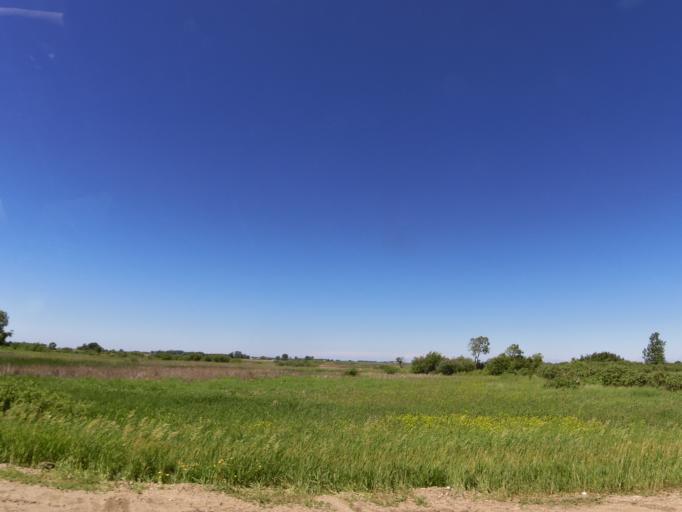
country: US
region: Minnesota
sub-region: Mahnomen County
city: Mahnomen
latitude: 47.1127
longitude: -95.9272
